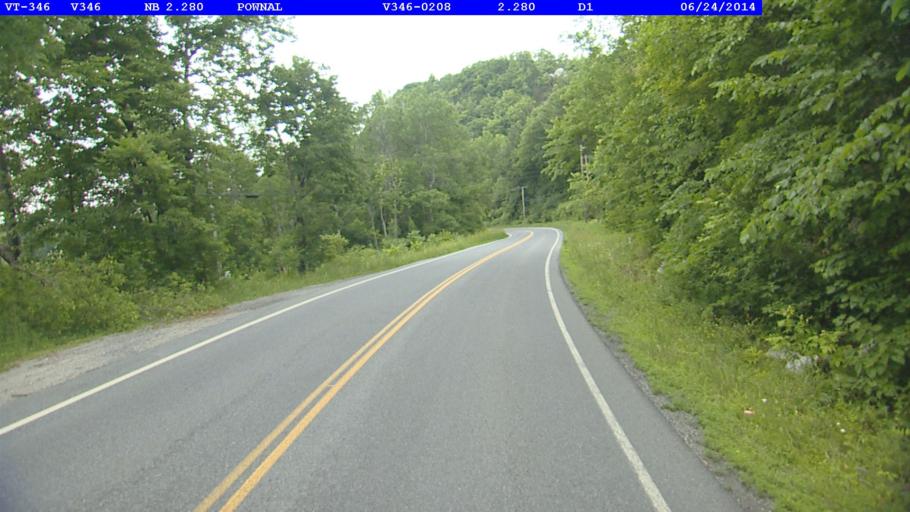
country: US
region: Massachusetts
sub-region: Berkshire County
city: Williamstown
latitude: 42.7904
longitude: -73.2550
